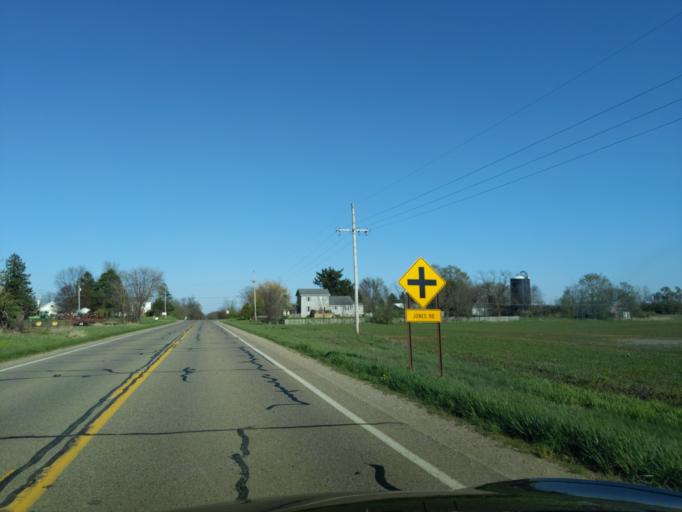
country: US
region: Michigan
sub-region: Eaton County
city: Grand Ledge
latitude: 42.8141
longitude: -84.8202
